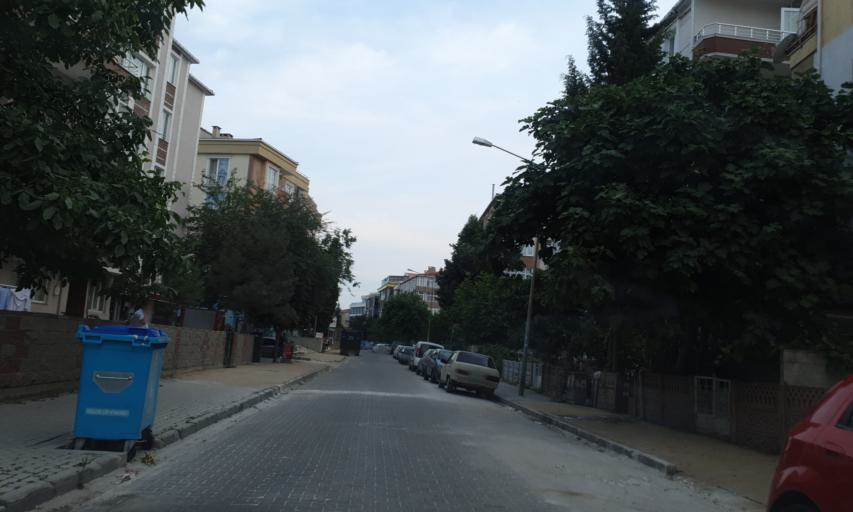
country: TR
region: Kirklareli
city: Luleburgaz
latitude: 41.4049
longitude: 27.3641
